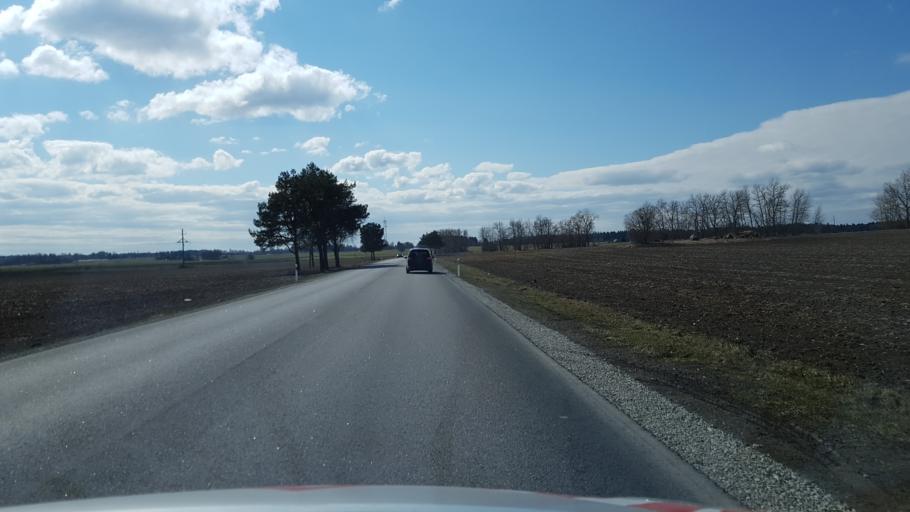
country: EE
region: Laeaene-Virumaa
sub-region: Rakvere linn
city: Rakvere
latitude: 59.3083
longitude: 26.3228
